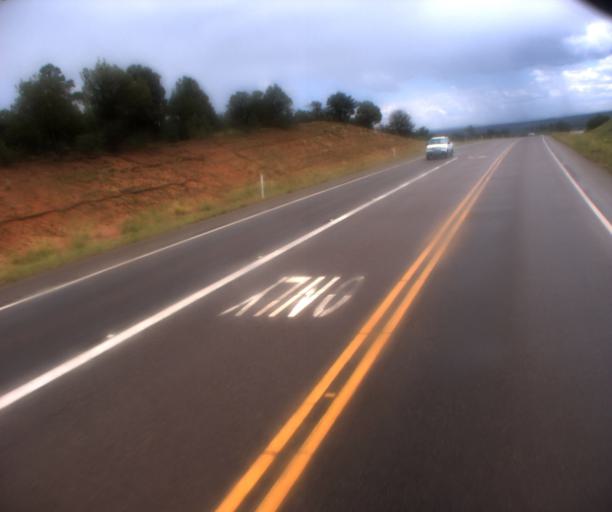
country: US
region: Arizona
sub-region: Navajo County
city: Heber-Overgaard
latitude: 34.3671
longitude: -110.3663
